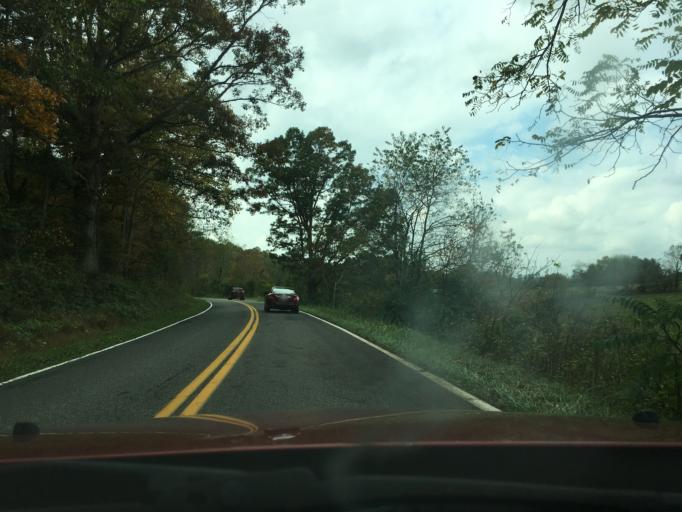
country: US
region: Virginia
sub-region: Pulaski County
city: Fairlawn
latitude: 37.1713
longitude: -80.6038
